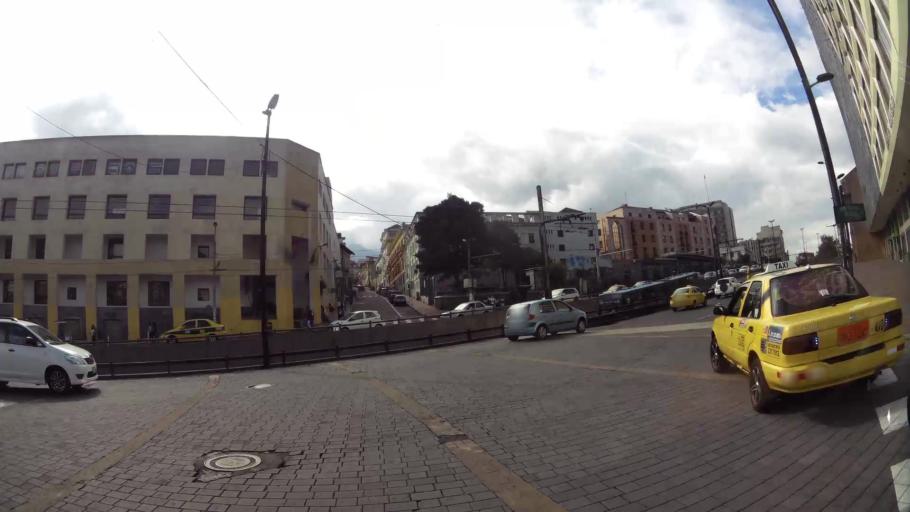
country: EC
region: Pichincha
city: Quito
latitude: -0.2176
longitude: -78.5054
